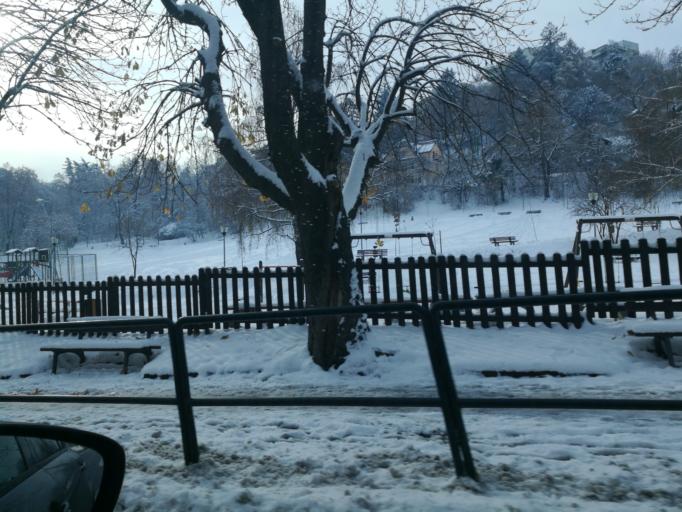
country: RO
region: Brasov
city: Brasov
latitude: 45.6473
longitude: 25.5852
